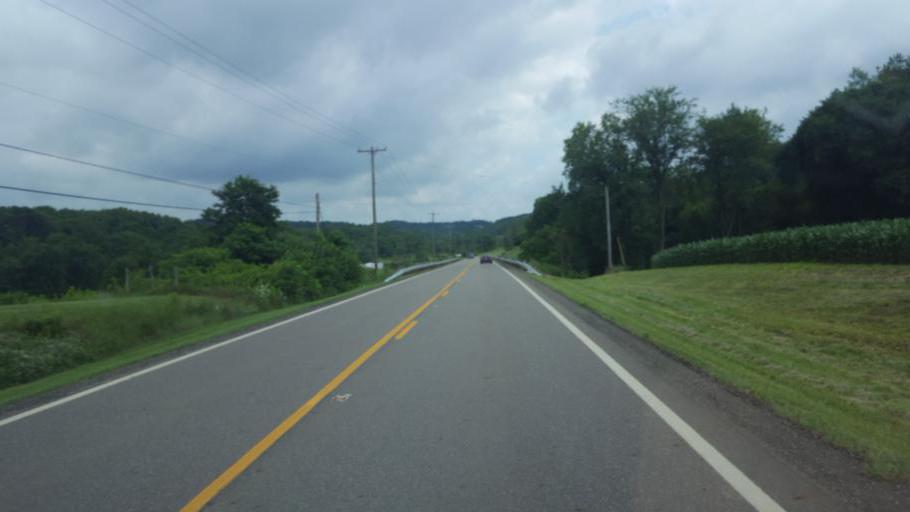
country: US
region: Ohio
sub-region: Columbiana County
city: Lisbon
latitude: 40.7306
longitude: -80.7898
